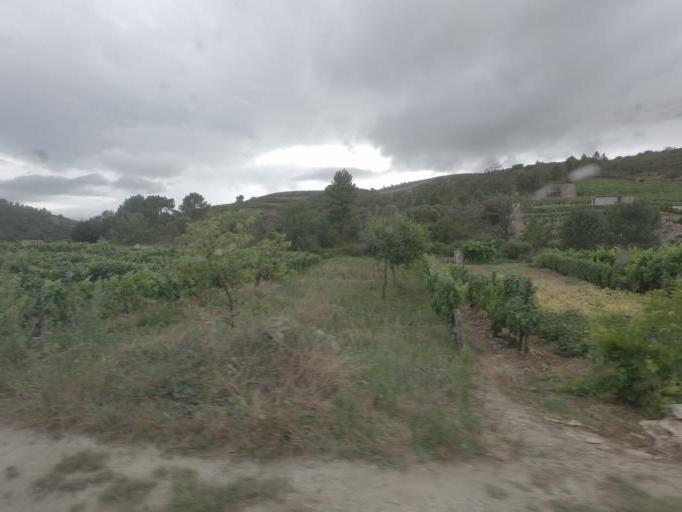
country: PT
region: Vila Real
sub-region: Sabrosa
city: Sabrosa
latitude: 41.2333
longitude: -7.4960
